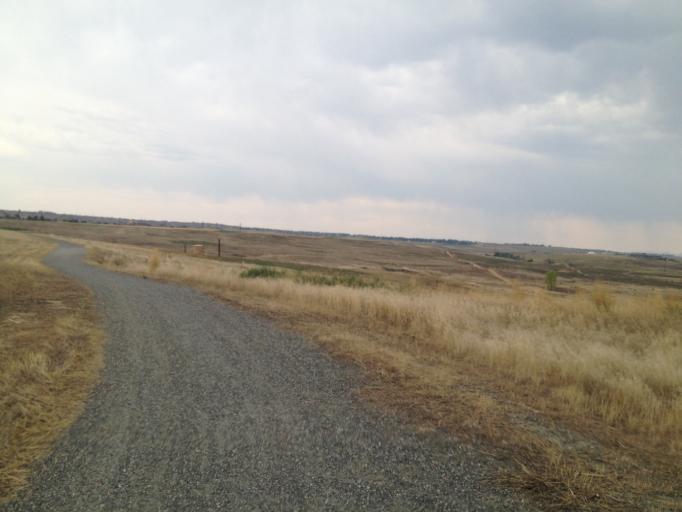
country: US
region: Colorado
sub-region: Boulder County
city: Lafayette
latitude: 39.9965
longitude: -105.0568
